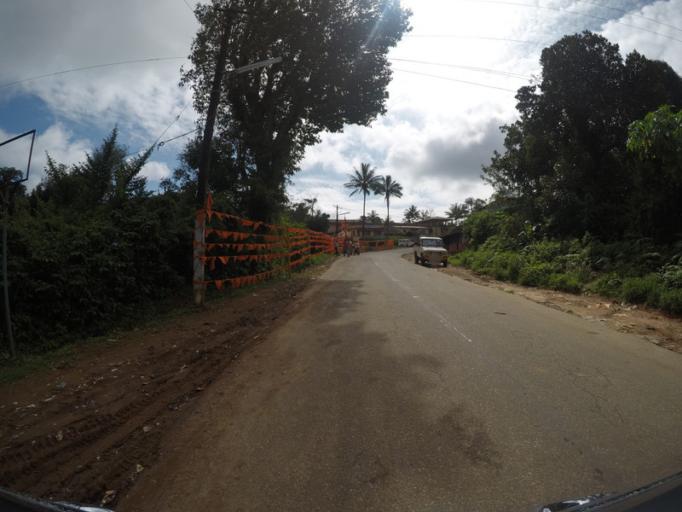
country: IN
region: Karnataka
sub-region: Kodagu
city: Madikeri
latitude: 12.4587
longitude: 75.7664
